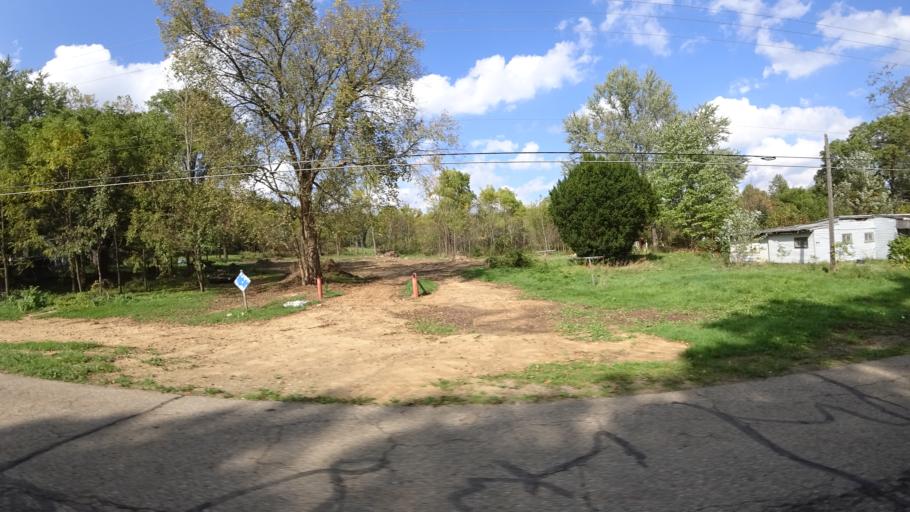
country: US
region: Michigan
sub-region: Branch County
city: Union City
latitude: 42.1043
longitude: -85.0387
